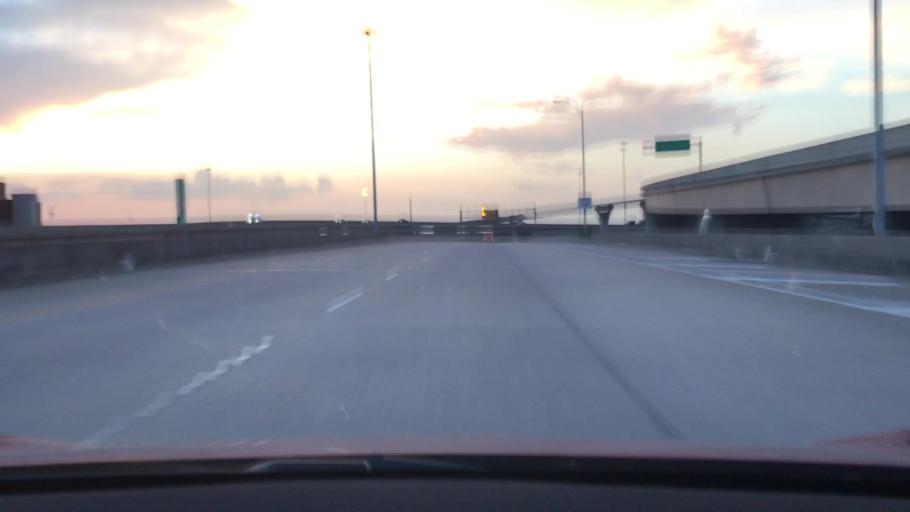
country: US
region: Louisiana
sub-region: Caddo Parish
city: Shreveport
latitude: 32.4936
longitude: -93.7572
